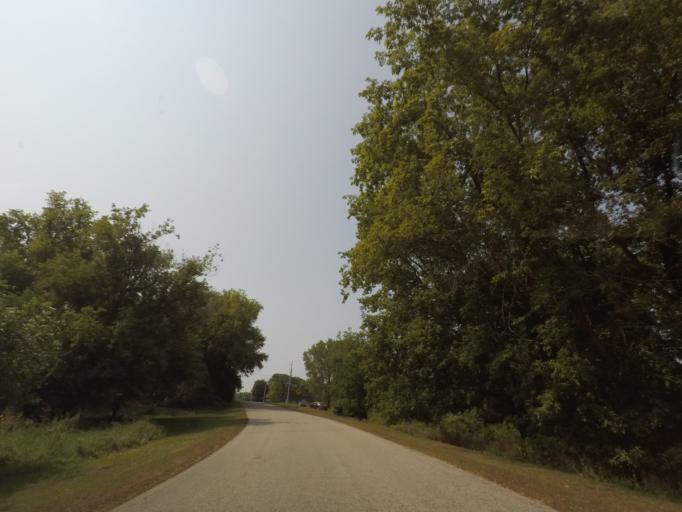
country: US
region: Wisconsin
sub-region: Jefferson County
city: Ixonia
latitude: 43.0701
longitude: -88.5831
